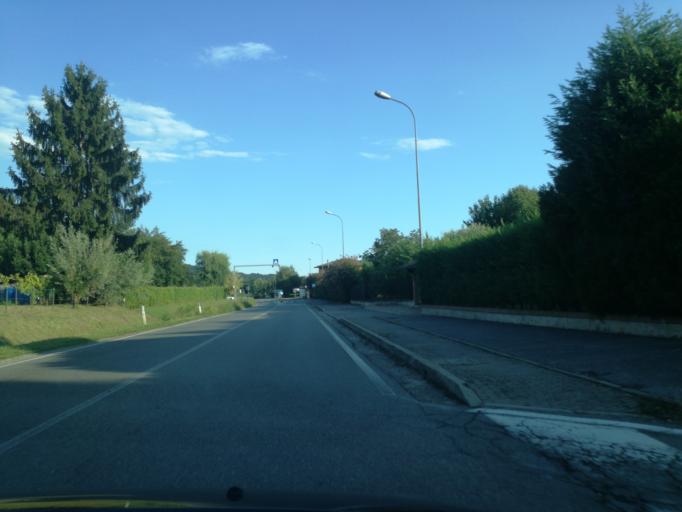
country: IT
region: Lombardy
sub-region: Provincia di Lecco
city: Arlate
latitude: 45.7246
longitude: 9.4433
